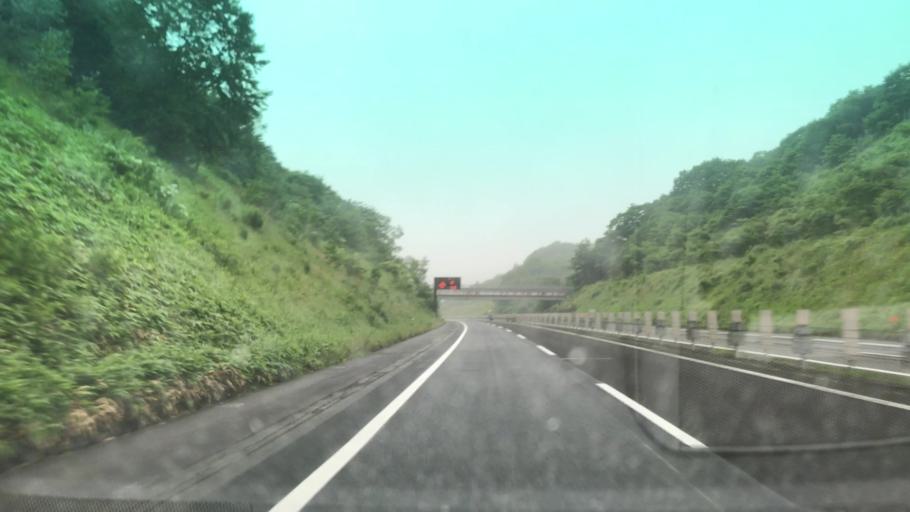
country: JP
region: Hokkaido
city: Tomakomai
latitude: 42.6366
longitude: 141.4974
